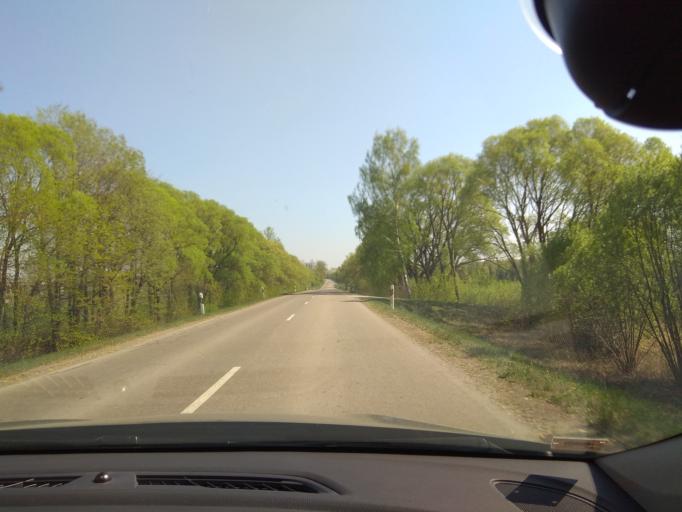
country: LT
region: Panevezys
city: Pasvalys
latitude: 55.9385
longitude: 24.2333
